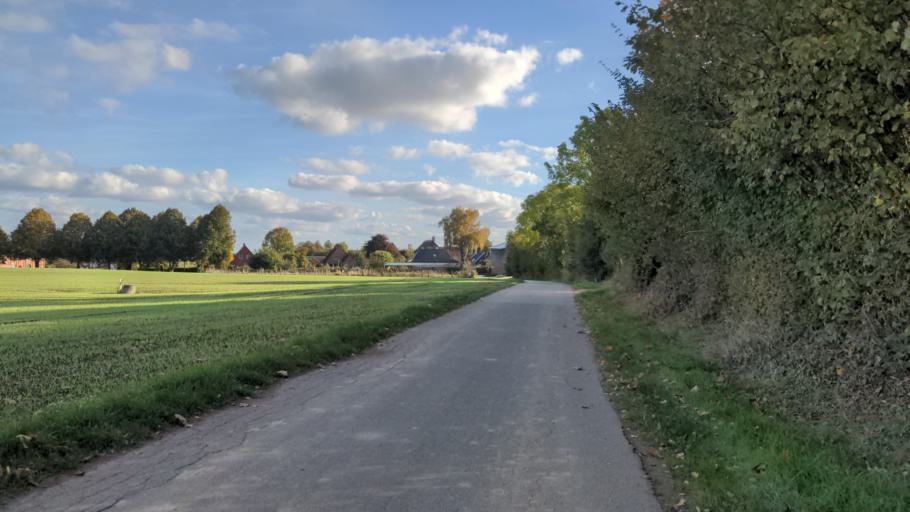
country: DE
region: Schleswig-Holstein
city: Schashagen
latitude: 54.1344
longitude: 10.9079
